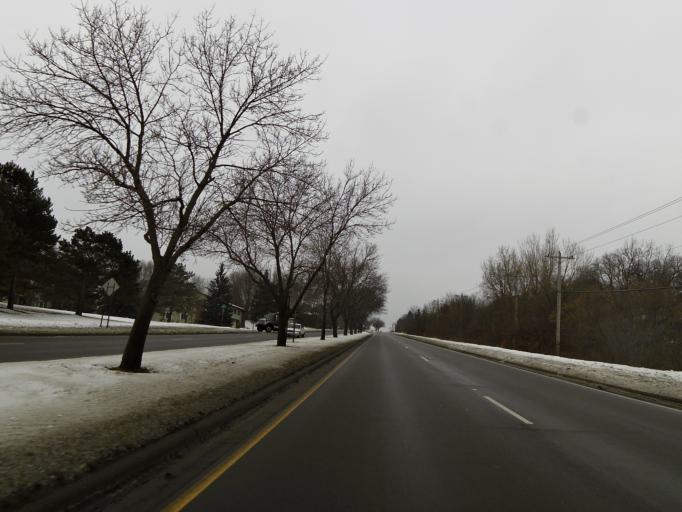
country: US
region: Minnesota
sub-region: Dakota County
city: Burnsville
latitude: 44.7558
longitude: -93.3031
